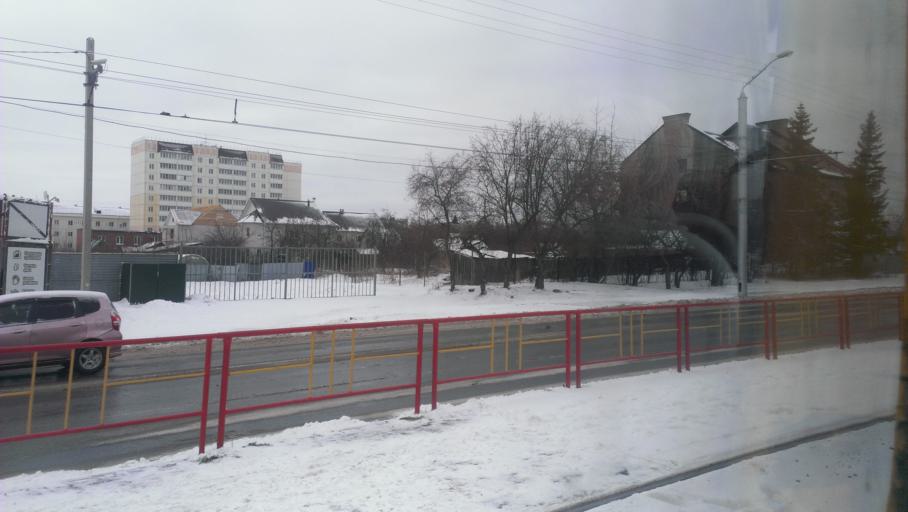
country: RU
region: Altai Krai
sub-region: Gorod Barnaulskiy
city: Barnaul
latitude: 53.3795
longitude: 83.7131
